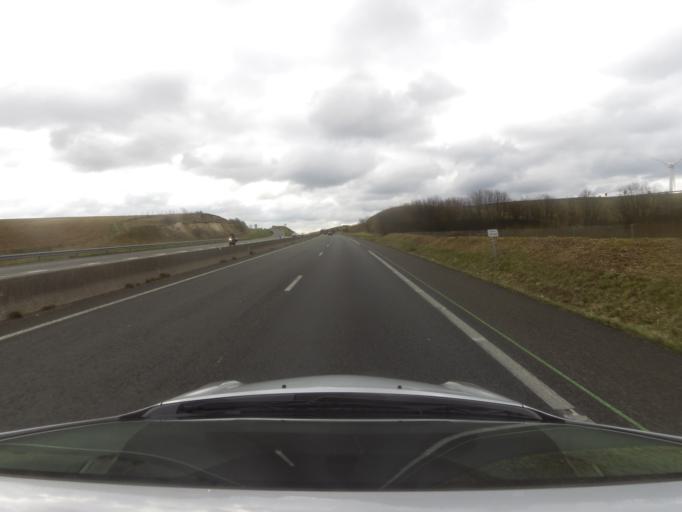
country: FR
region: Nord-Pas-de-Calais
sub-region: Departement du Pas-de-Calais
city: Dannes
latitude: 50.5790
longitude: 1.6417
